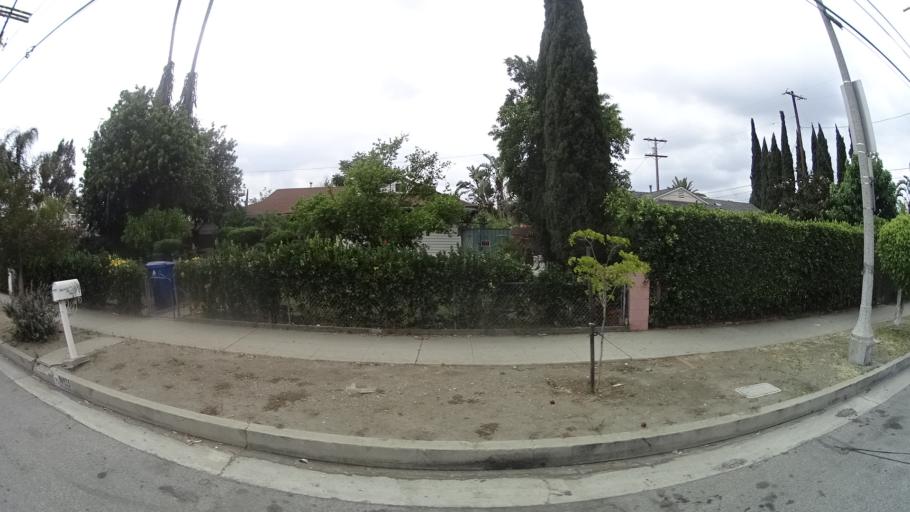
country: US
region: California
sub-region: Los Angeles County
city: San Fernando
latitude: 34.2522
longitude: -118.4413
